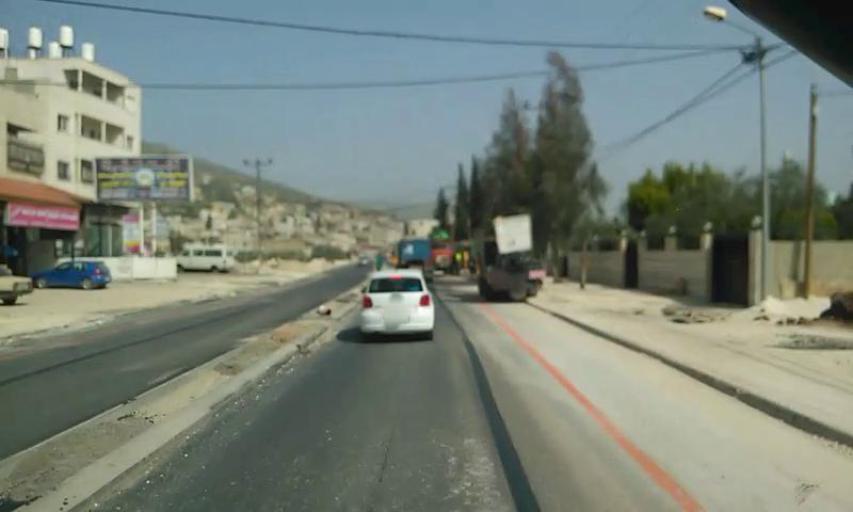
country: PS
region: West Bank
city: Huwwarah
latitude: 32.1436
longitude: 35.2581
